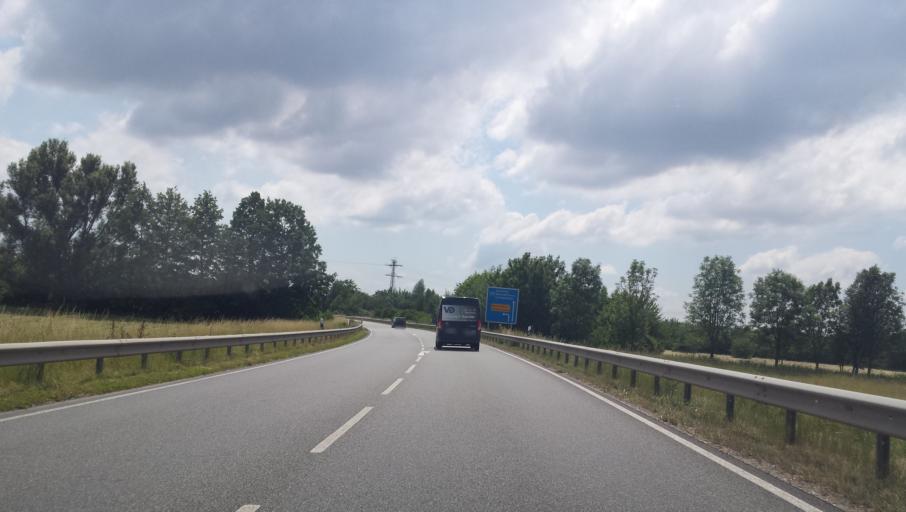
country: DE
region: Rheinland-Pfalz
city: Ruppertsberg
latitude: 49.4018
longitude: 8.2063
